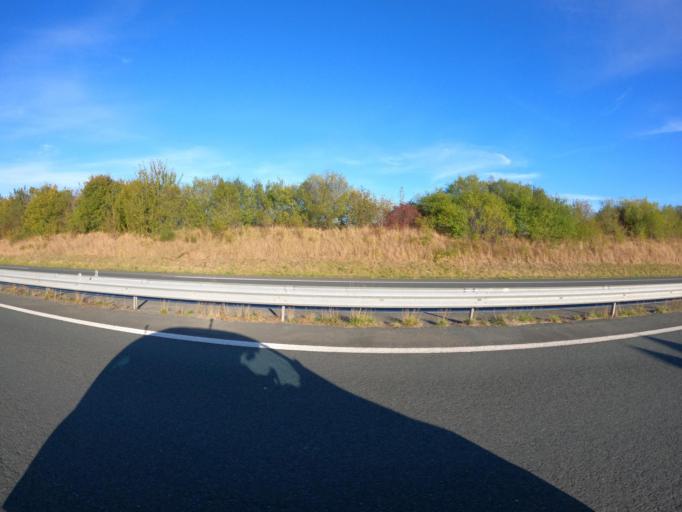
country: FR
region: Pays de la Loire
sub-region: Departement de Maine-et-Loire
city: Mazieres-en-Mauges
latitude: 47.0752
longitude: -0.8262
